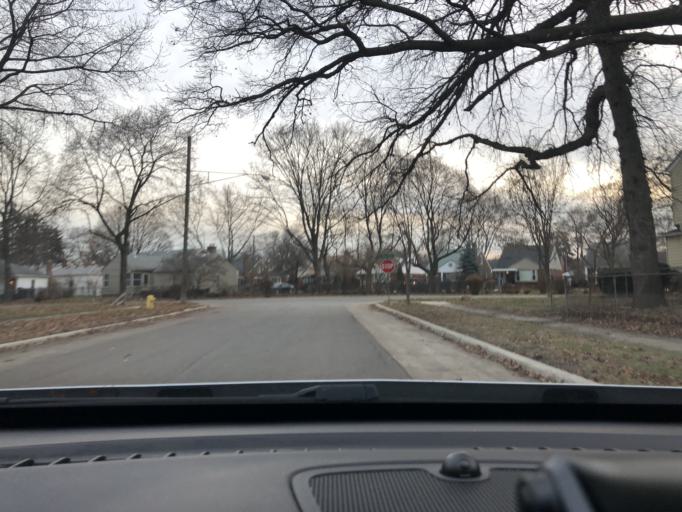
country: US
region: Michigan
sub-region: Wayne County
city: Allen Park
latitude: 42.2849
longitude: -83.2286
